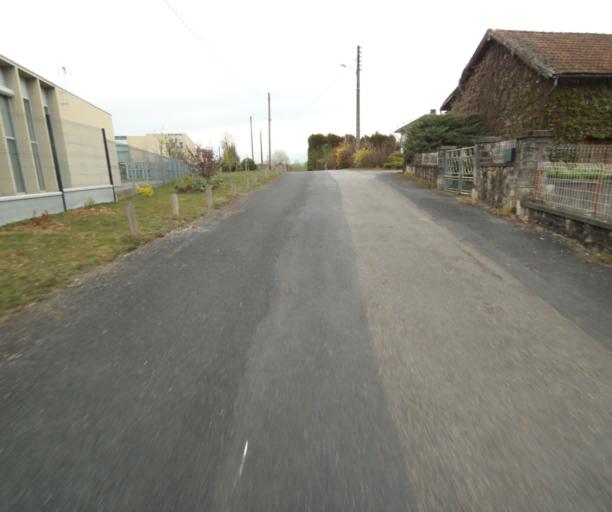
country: FR
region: Limousin
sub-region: Departement de la Correze
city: Tulle
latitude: 45.2564
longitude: 1.7694
